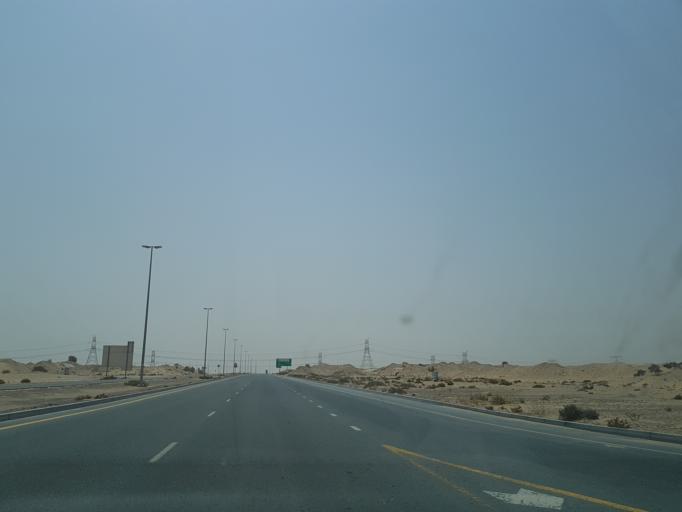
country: AE
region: Dubai
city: Dubai
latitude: 25.0547
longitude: 55.3040
